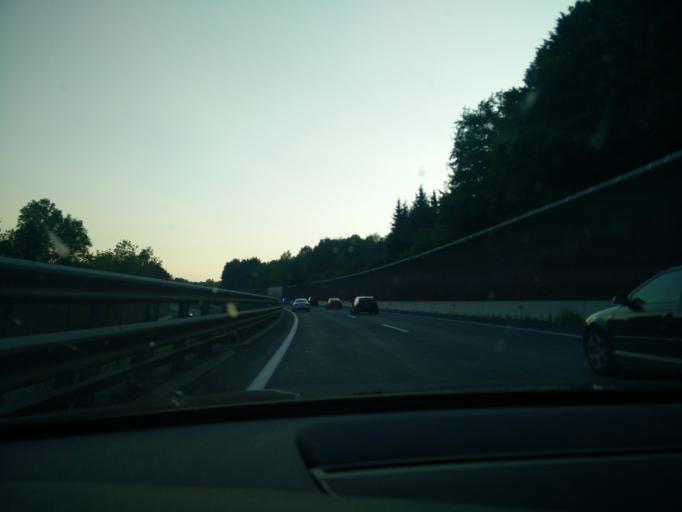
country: AT
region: Carinthia
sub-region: Politischer Bezirk Villach Land
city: Velden am Woerthersee
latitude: 46.6245
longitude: 14.0526
